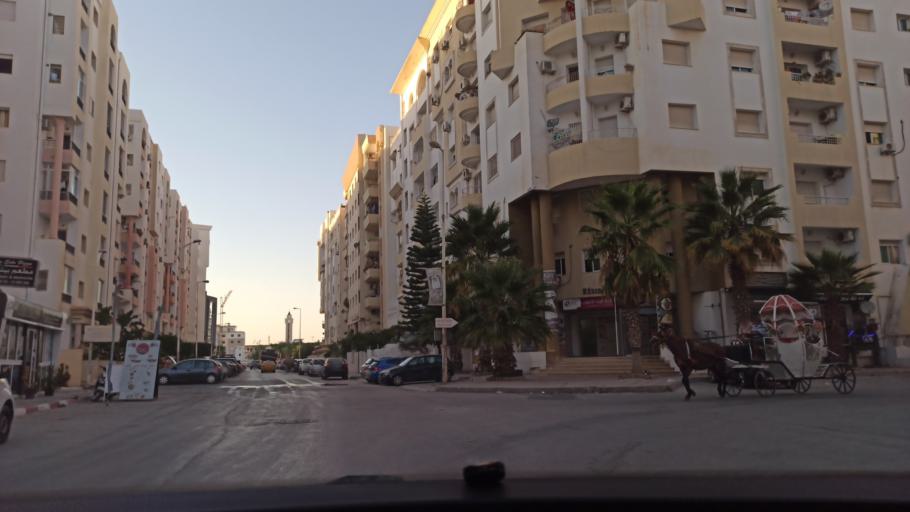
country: TN
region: Tunis
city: La Goulette
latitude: 36.8608
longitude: 10.2660
